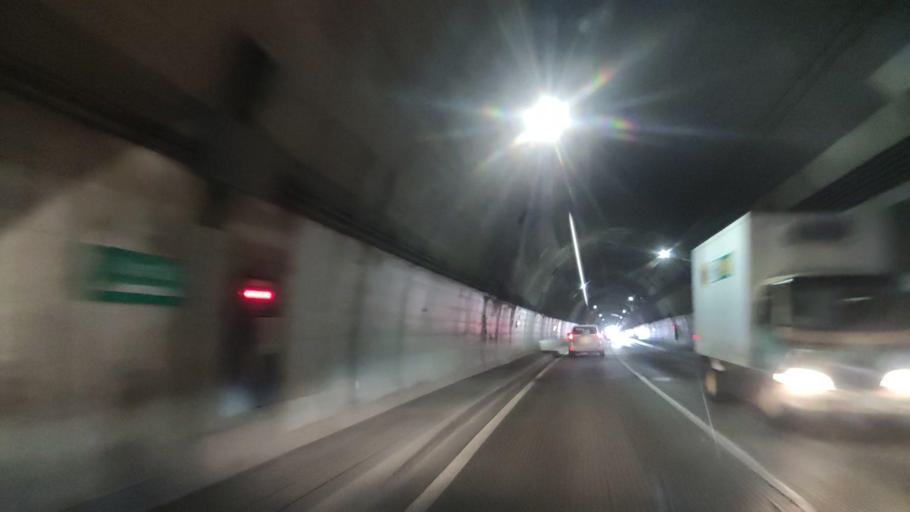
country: JP
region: Hokkaido
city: Ishikari
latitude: 43.4431
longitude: 141.4136
